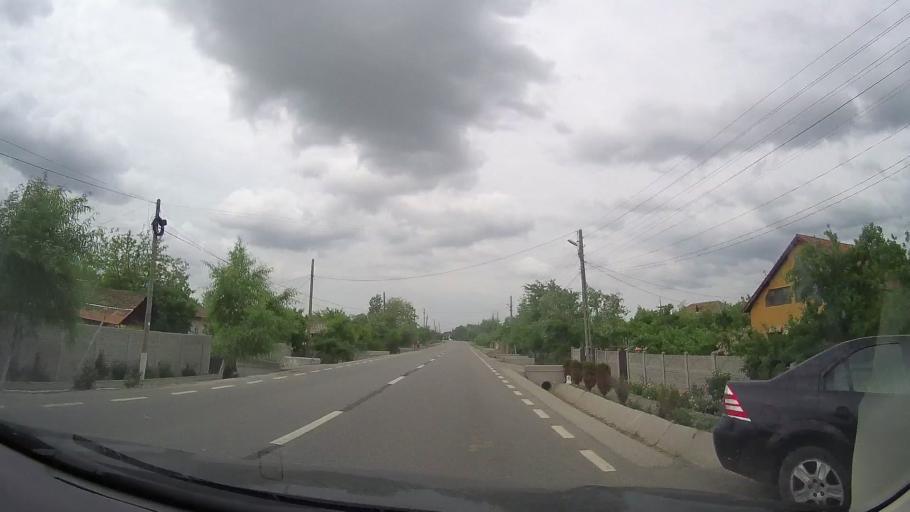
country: RO
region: Dolj
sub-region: Comuna Leu
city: Leu
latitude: 44.1864
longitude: 24.0109
